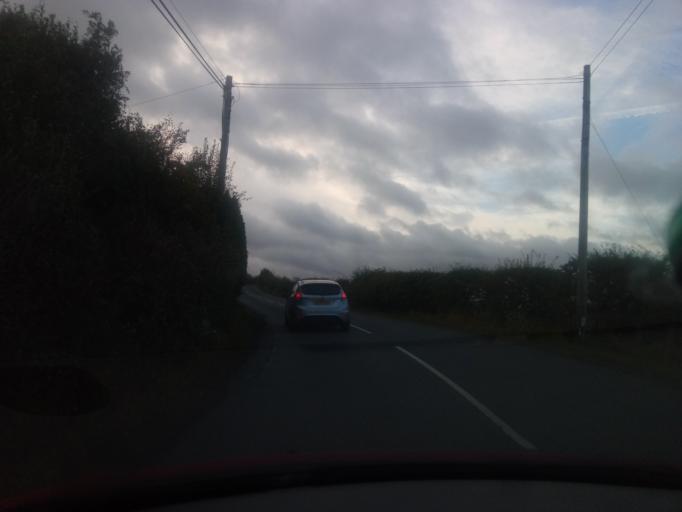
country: GB
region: Scotland
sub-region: The Scottish Borders
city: Jedburgh
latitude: 55.3950
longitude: -2.6495
